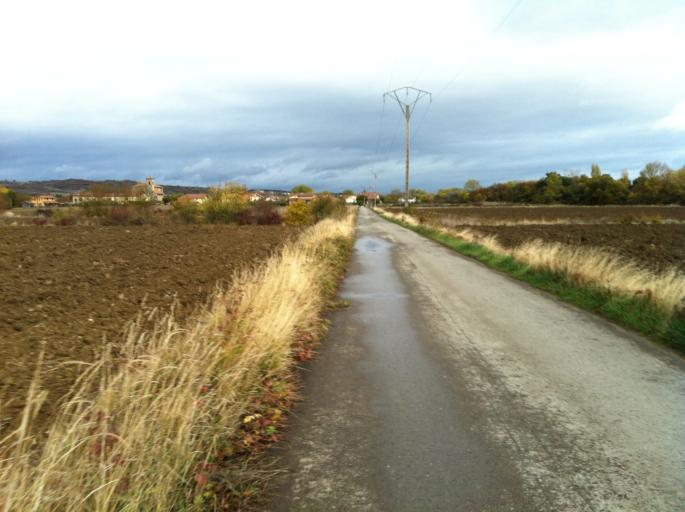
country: ES
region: Basque Country
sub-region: Provincia de Alava
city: Gasteiz / Vitoria
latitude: 42.8748
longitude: -2.7066
